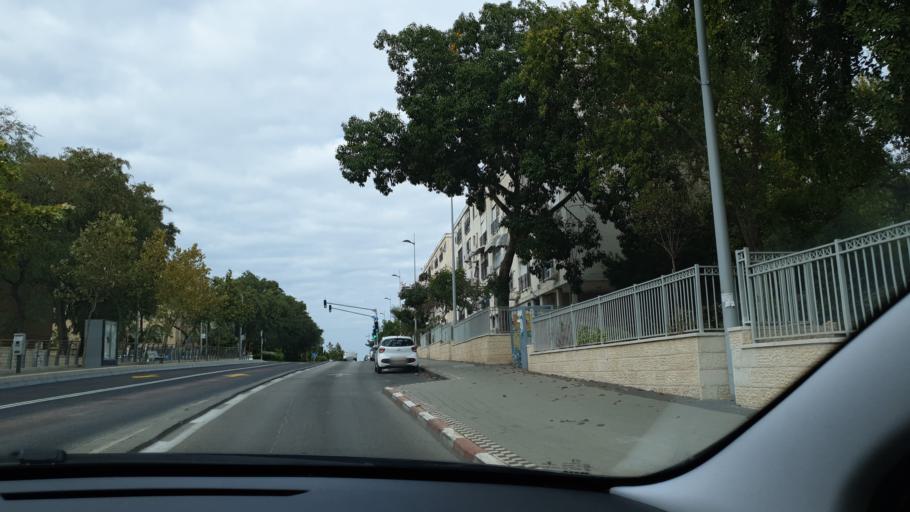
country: IL
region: Haifa
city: Qiryat Ata
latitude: 32.8085
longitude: 35.1172
